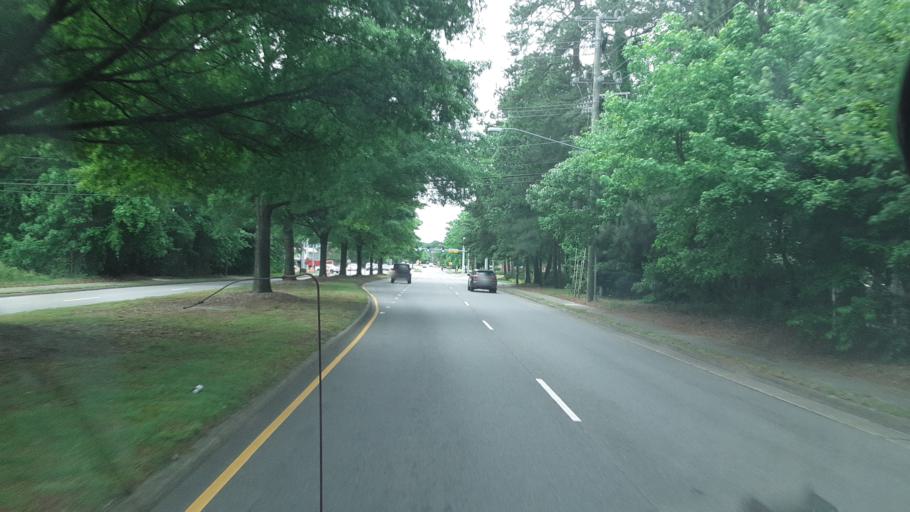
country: US
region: Virginia
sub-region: City of Virginia Beach
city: Virginia Beach
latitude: 36.7615
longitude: -76.0171
